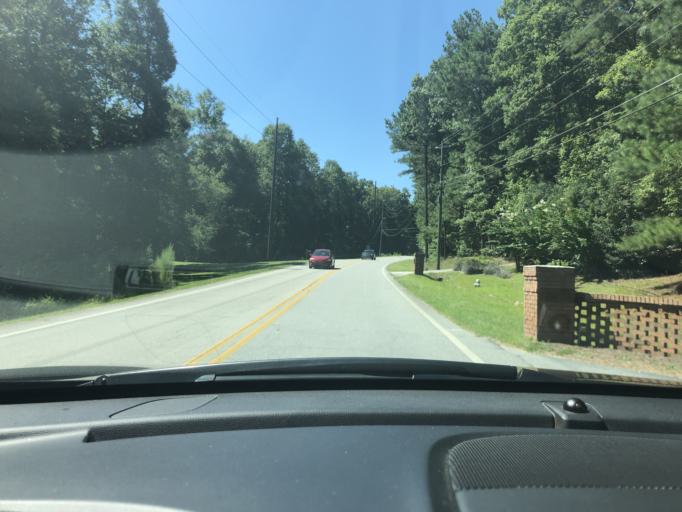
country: US
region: Georgia
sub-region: Gwinnett County
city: Grayson
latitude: 33.9235
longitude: -83.9492
